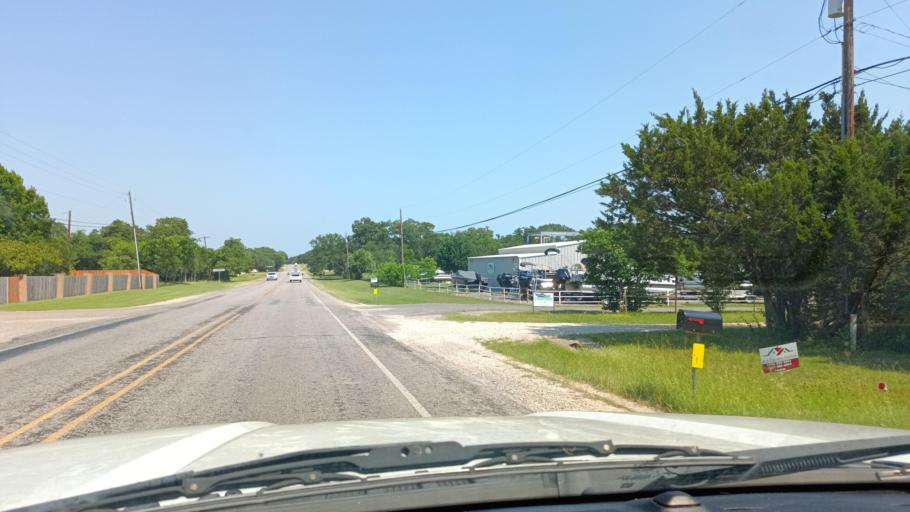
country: US
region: Texas
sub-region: Bell County
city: Morgans Point Resort
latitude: 31.1037
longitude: -97.4995
